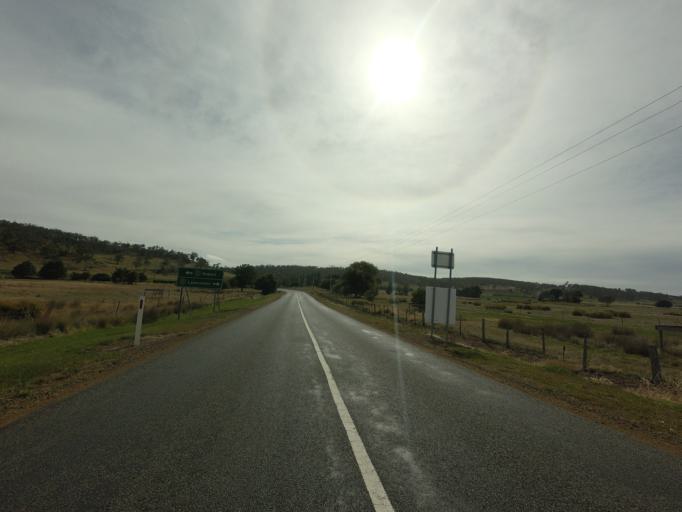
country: AU
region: Tasmania
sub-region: Brighton
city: Bridgewater
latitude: -42.2959
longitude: 147.3844
